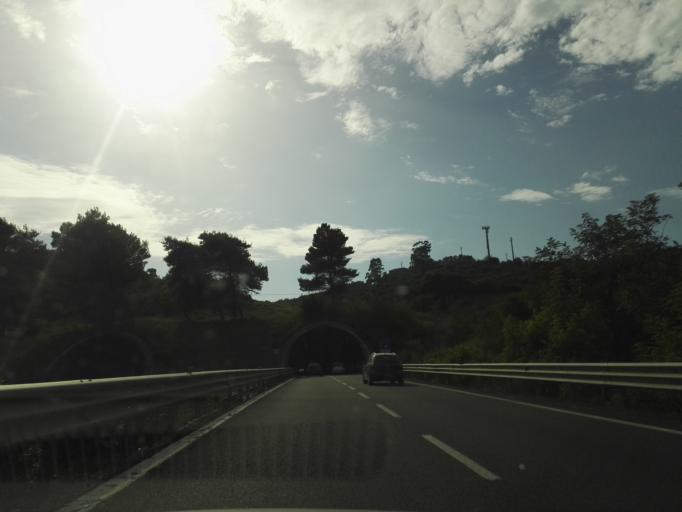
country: IT
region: Calabria
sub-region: Provincia di Catanzaro
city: Marcellinara
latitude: 38.9178
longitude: 16.4830
